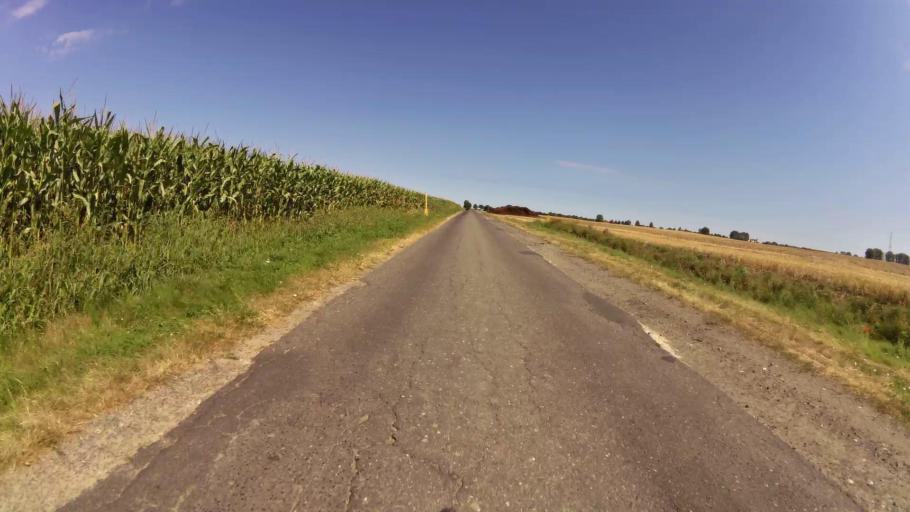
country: PL
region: West Pomeranian Voivodeship
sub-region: Powiat stargardzki
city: Dobrzany
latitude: 53.2657
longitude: 15.4396
